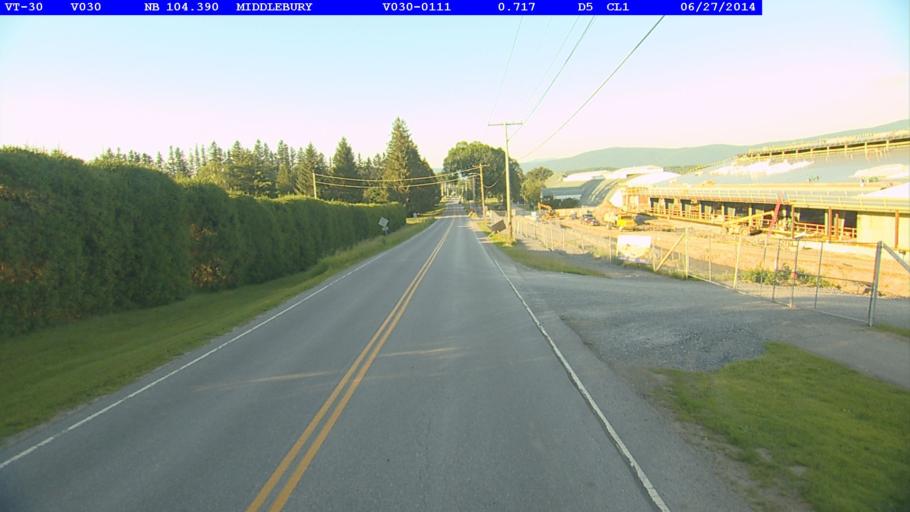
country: US
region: Vermont
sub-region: Addison County
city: Middlebury (village)
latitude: 44.0032
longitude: -73.1800
